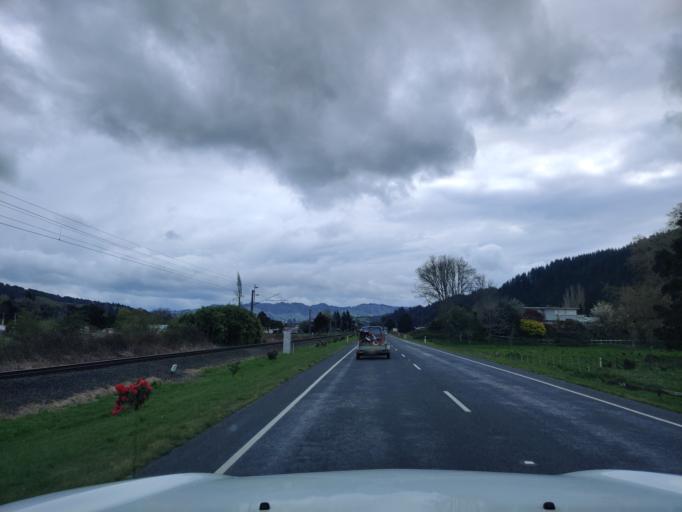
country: NZ
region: Waikato
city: Turangi
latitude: -38.8815
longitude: 175.2904
